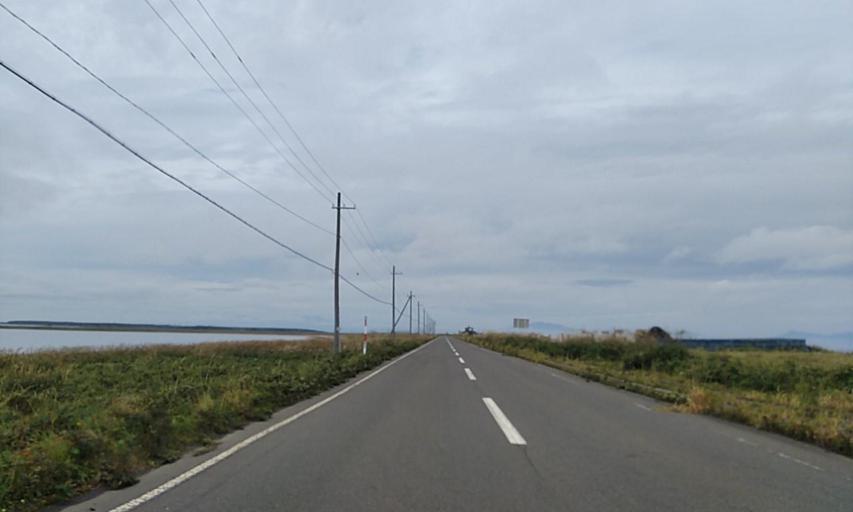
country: JP
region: Hokkaido
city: Shibetsu
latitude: 43.5935
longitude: 145.3295
